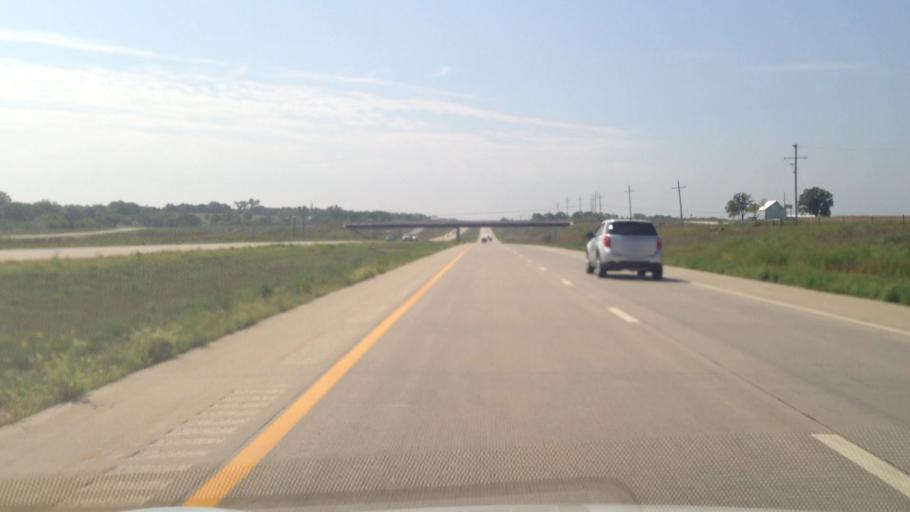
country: US
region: Kansas
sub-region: Douglas County
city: Baldwin City
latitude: 38.8224
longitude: -95.2691
